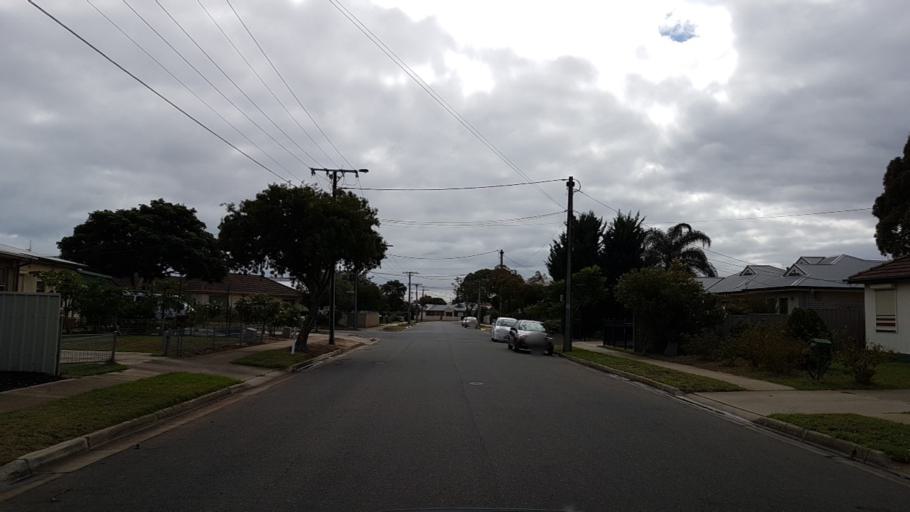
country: AU
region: South Australia
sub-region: Charles Sturt
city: Seaton
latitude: -34.9085
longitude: 138.5205
